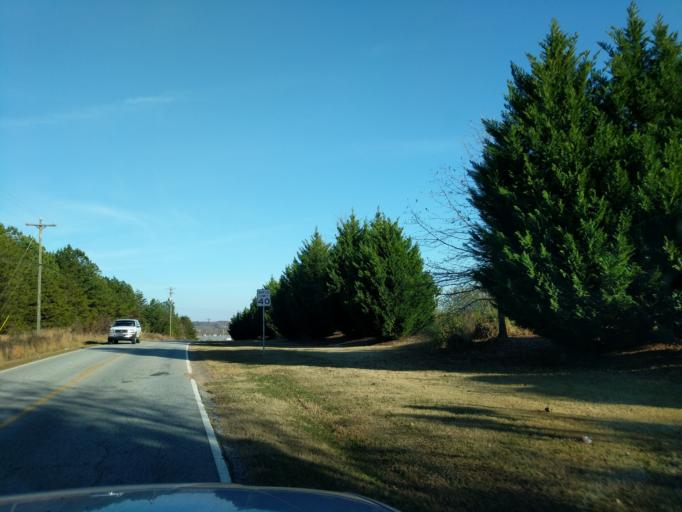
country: US
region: South Carolina
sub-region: Spartanburg County
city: Wellford
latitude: 34.9073
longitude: -82.0938
